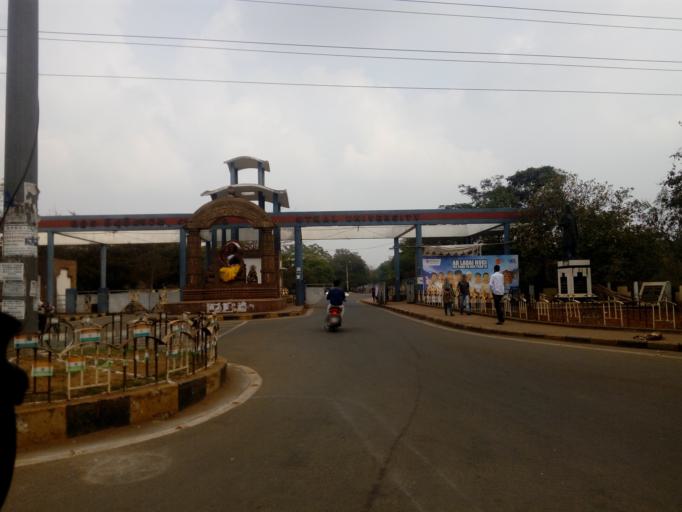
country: IN
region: Odisha
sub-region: Khordha
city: Bhubaneshwar
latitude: 20.2967
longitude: 85.8405
